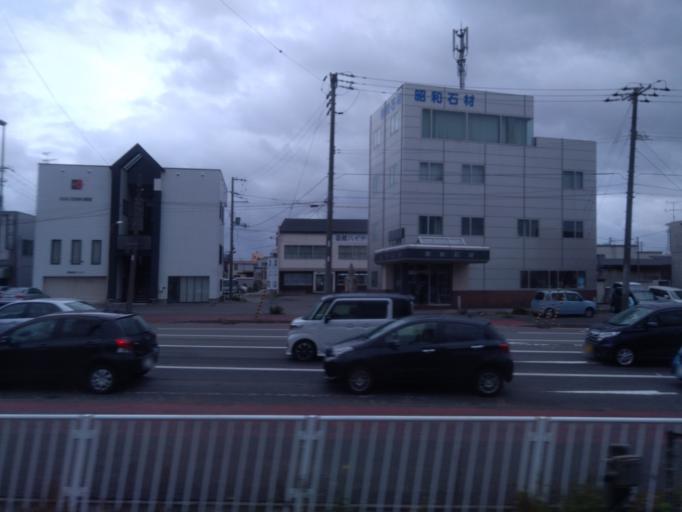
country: JP
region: Hokkaido
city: Hakodate
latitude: 41.8002
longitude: 140.7340
